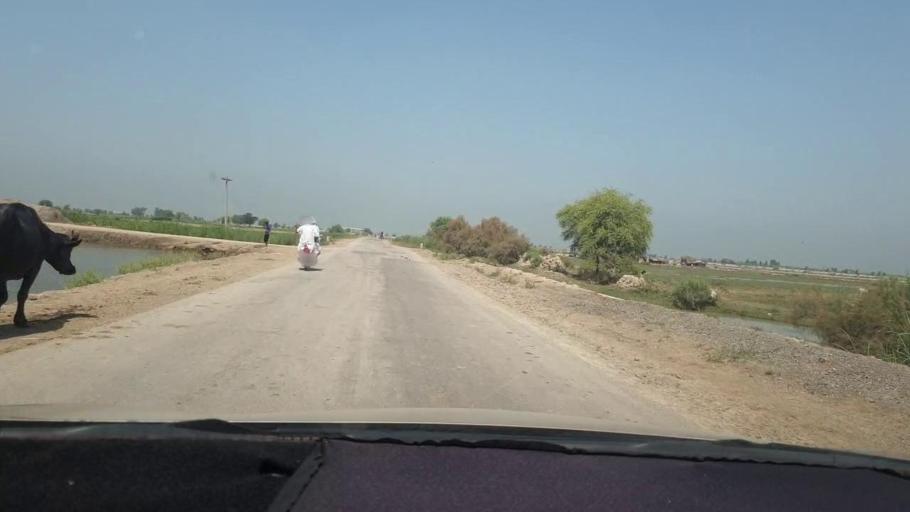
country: PK
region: Sindh
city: Shahdadkot
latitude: 27.8410
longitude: 68.0068
